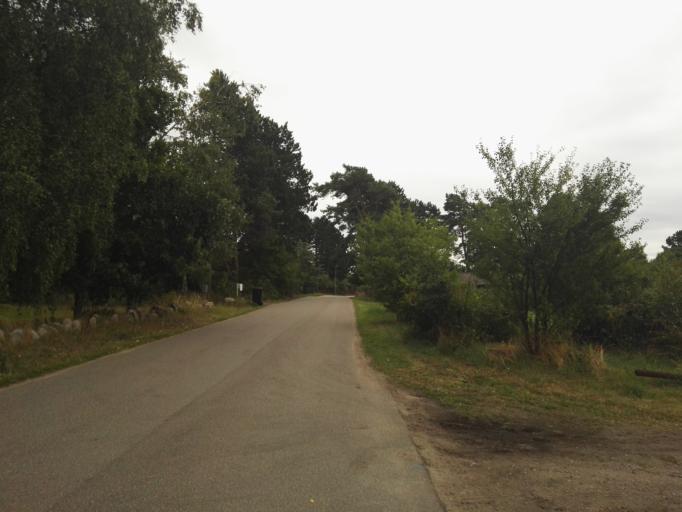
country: DK
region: Zealand
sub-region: Odsherred Kommune
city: Nykobing Sjaelland
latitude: 55.9361
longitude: 11.6659
